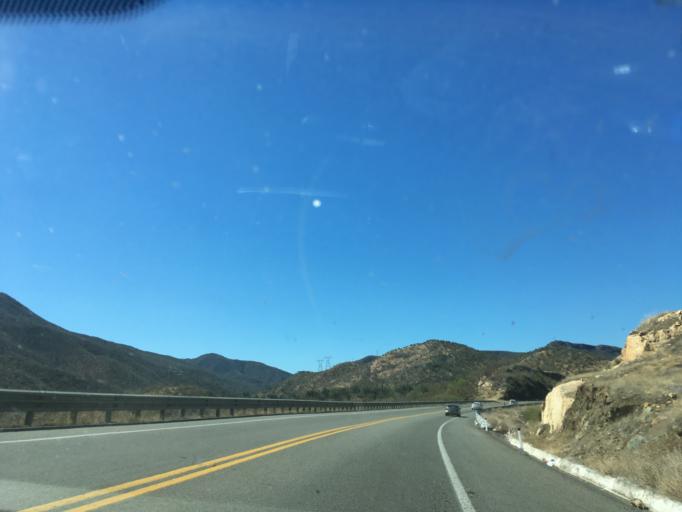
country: MX
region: Michoacan
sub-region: Arteaga
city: Infiernillo (Morelos de Infiernillo)
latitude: 18.4211
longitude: -101.9079
